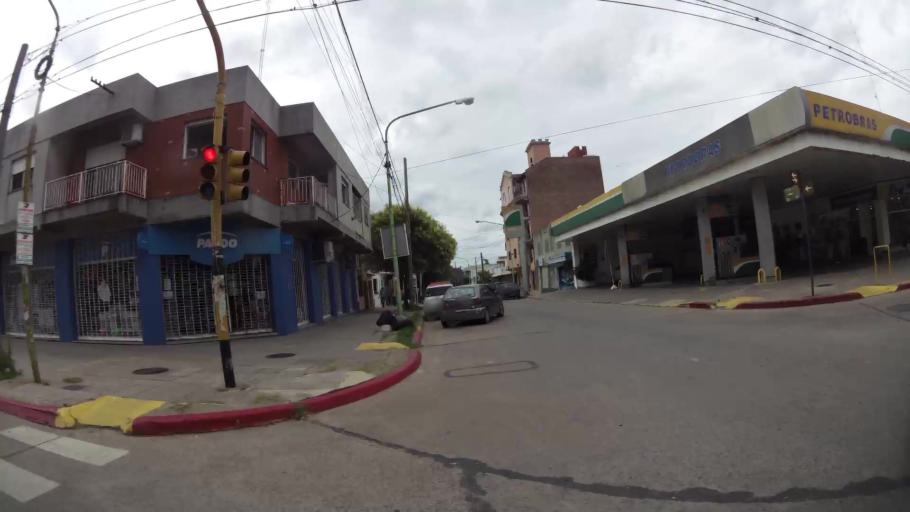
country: AR
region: Buenos Aires
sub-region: Partido de Campana
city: Campana
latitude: -34.1630
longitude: -58.9627
